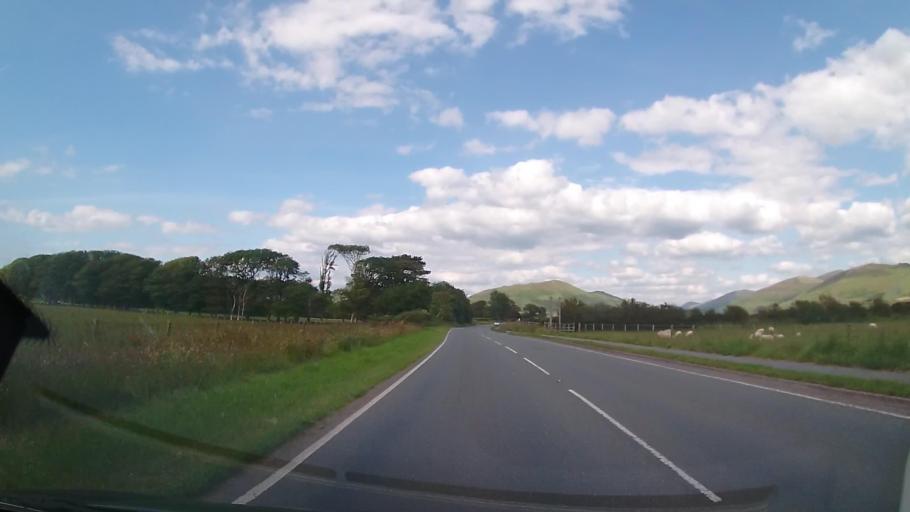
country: GB
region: Wales
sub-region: Gwynedd
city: Tywyn
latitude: 52.5945
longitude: -4.0719
